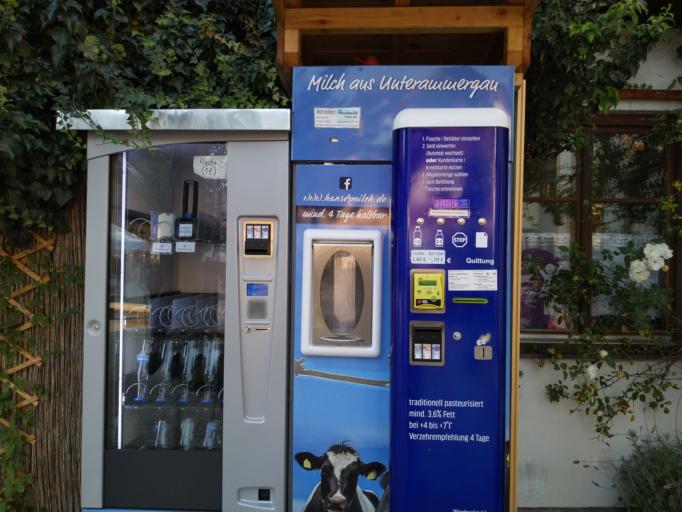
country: DE
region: Bavaria
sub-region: Upper Bavaria
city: Oberammergau
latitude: 47.5974
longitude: 11.0640
